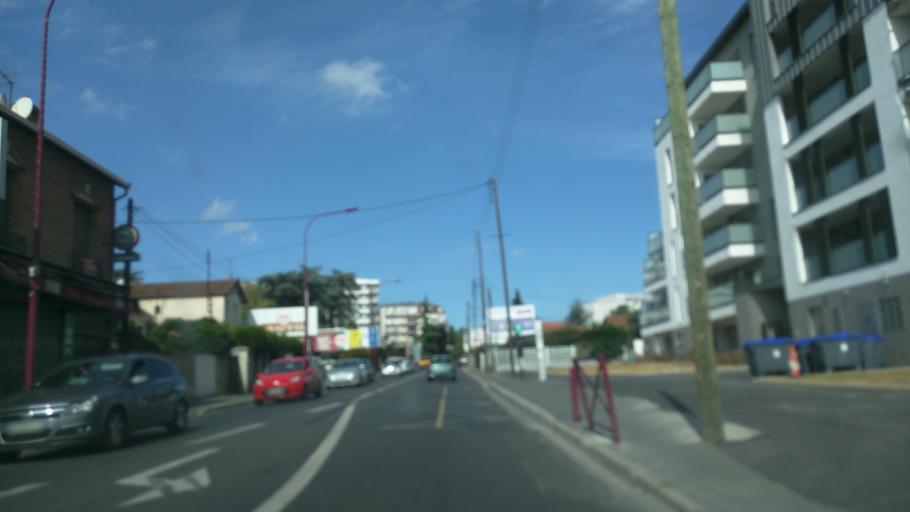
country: FR
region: Ile-de-France
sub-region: Departement du Val-d'Oise
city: Bezons
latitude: 48.9345
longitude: 2.2090
